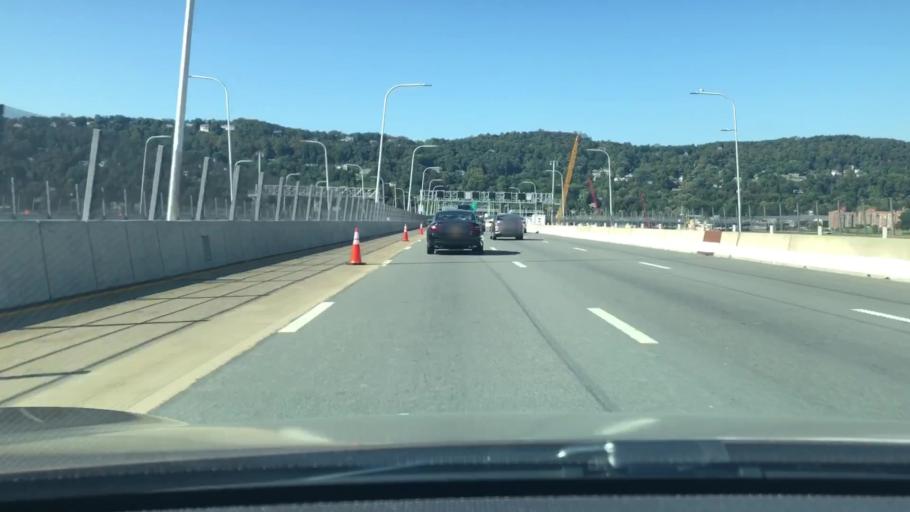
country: US
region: New York
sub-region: Rockland County
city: South Nyack
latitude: 41.0712
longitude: -73.9056
